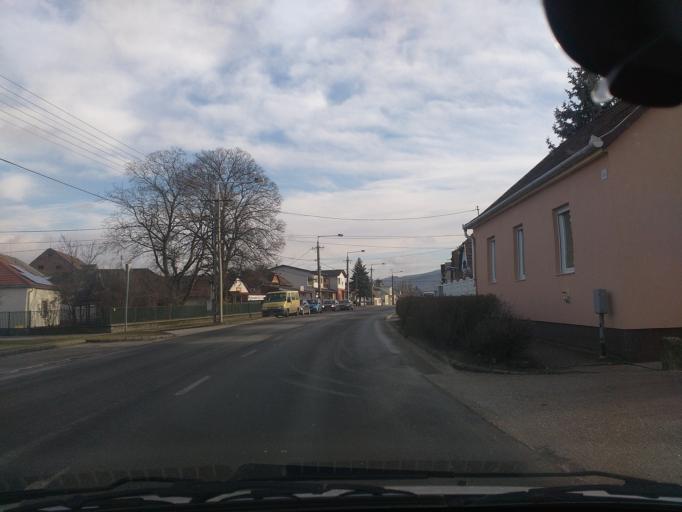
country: HU
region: Komarom-Esztergom
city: Tat
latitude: 47.7438
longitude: 18.6469
